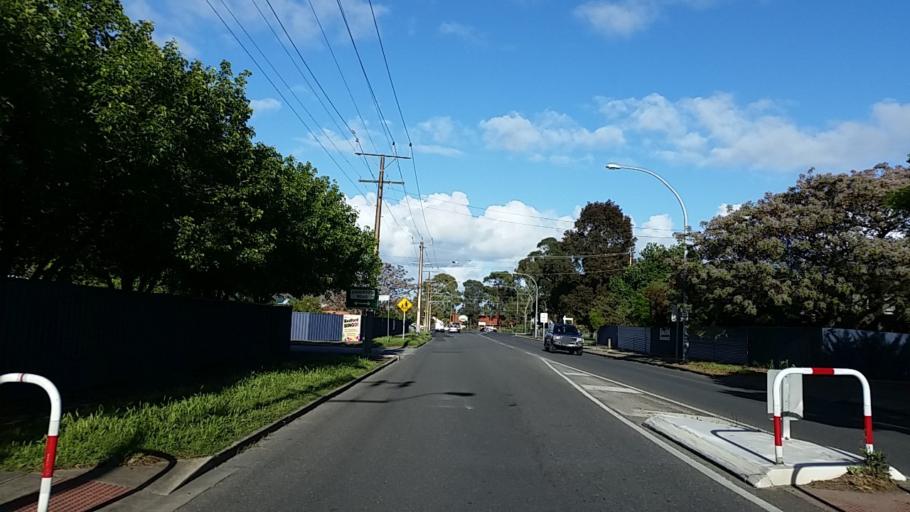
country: AU
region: South Australia
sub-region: Mitcham
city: Clapham
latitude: -34.9907
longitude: 138.5948
